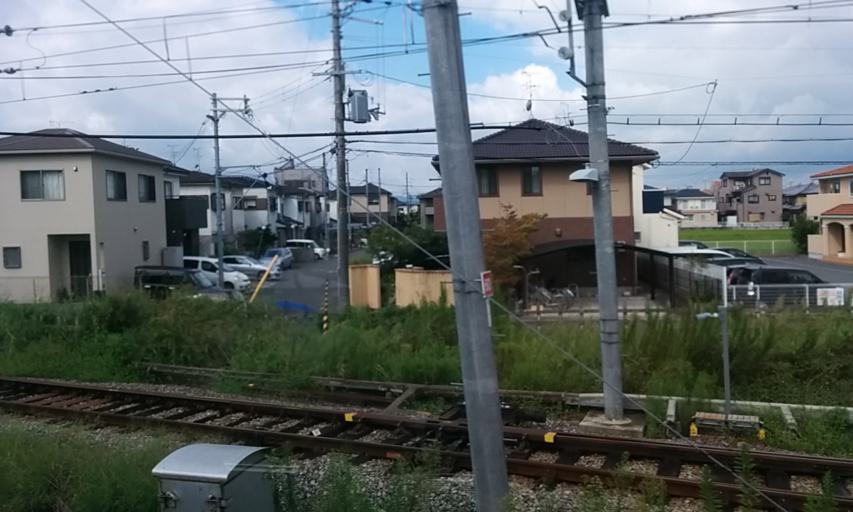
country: JP
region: Nara
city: Kashihara-shi
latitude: 34.5239
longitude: 135.7947
